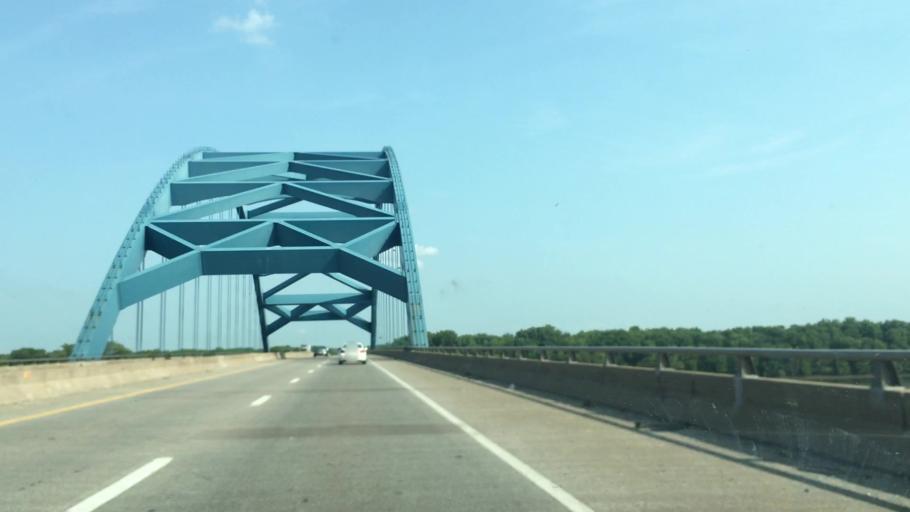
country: US
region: Illinois
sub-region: Rock Island County
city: Rock Island
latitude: 41.4799
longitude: -90.6337
